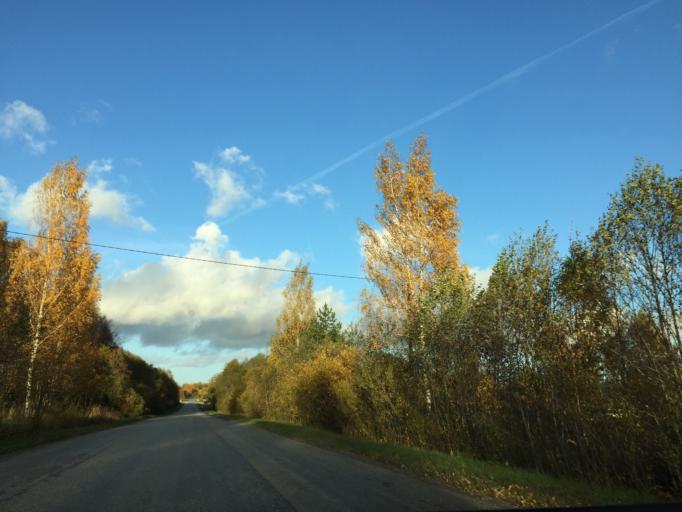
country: LV
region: Ogre
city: Jumprava
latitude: 56.7932
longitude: 25.0388
